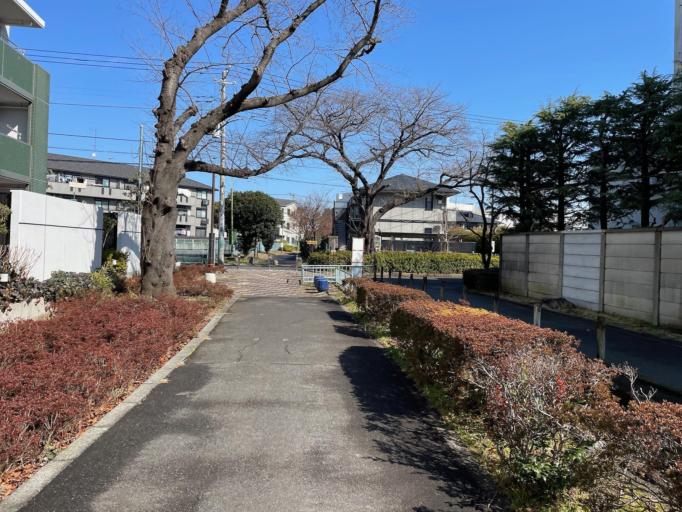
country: JP
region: Tokyo
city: Kokubunji
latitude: 35.6589
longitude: 139.4965
